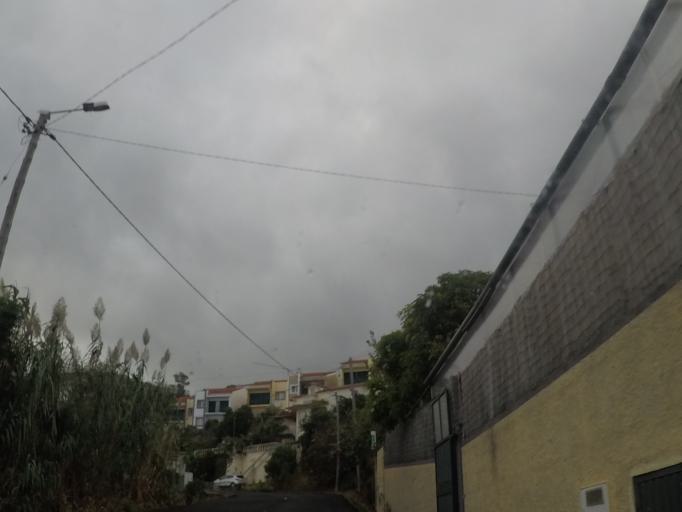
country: PT
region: Madeira
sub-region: Machico
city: Machico
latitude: 32.7069
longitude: -16.7736
